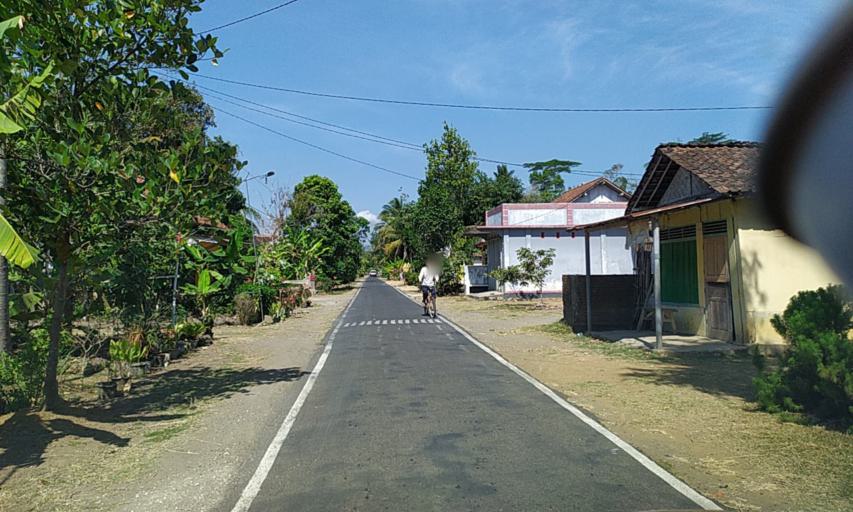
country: ID
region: Central Java
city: Kroya
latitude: -7.6797
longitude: 109.3439
